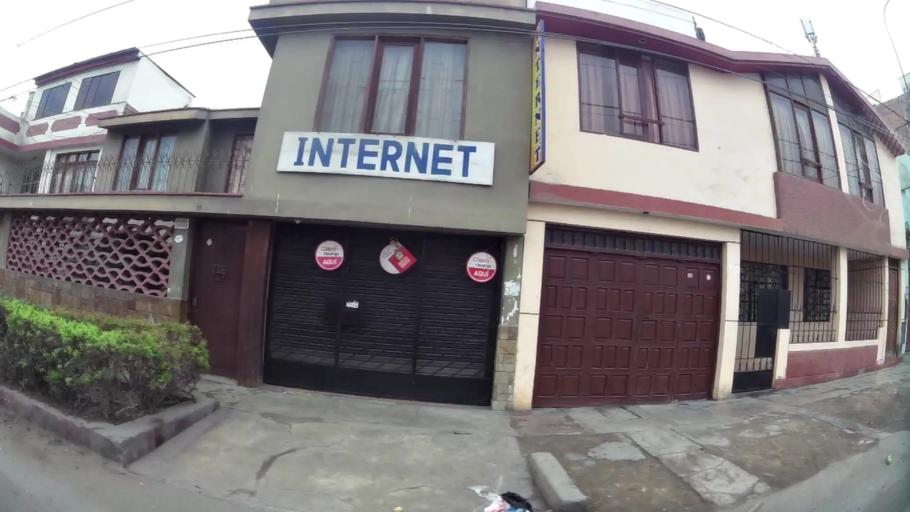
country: PE
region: Lima
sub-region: Lima
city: Surco
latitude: -12.1608
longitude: -76.9738
